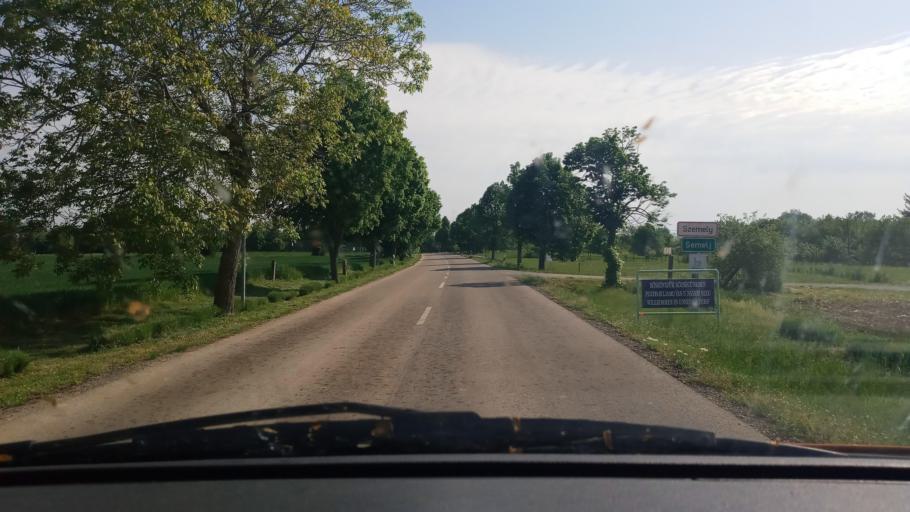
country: HU
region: Baranya
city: Kozarmisleny
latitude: 46.0049
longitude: 18.3176
